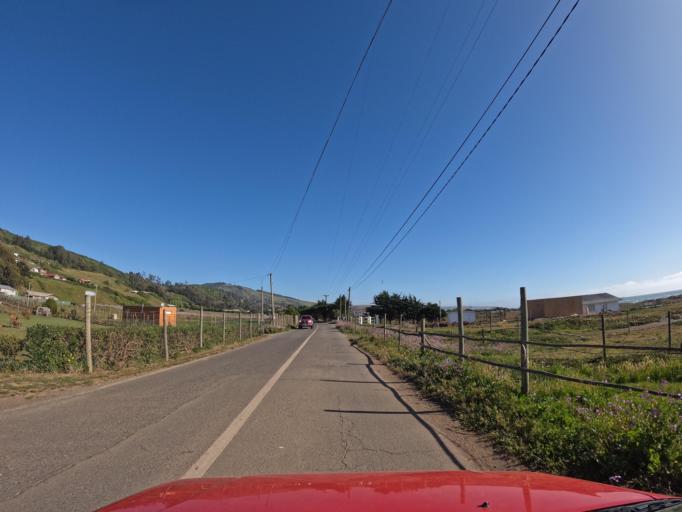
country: CL
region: Maule
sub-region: Provincia de Talca
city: Constitucion
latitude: -34.8407
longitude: -72.1427
